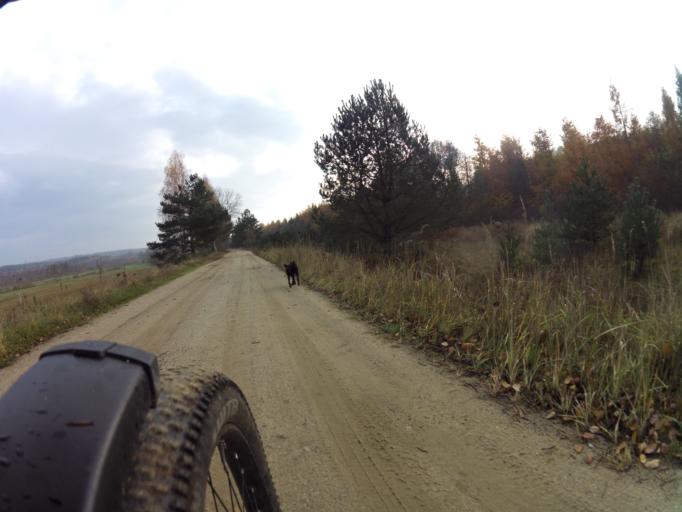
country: PL
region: Pomeranian Voivodeship
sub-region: Powiat wejherowski
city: Gniewino
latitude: 54.7043
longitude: 18.1051
